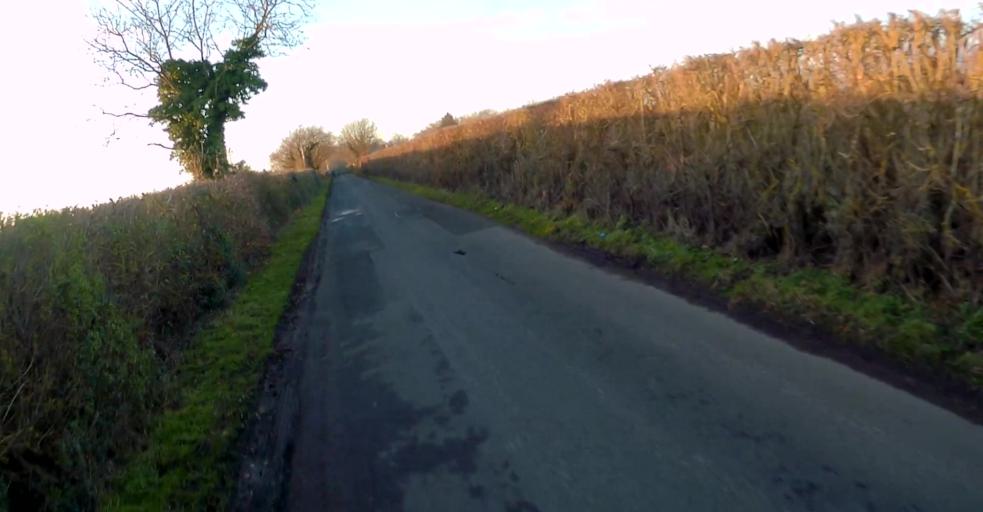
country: GB
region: England
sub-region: West Berkshire
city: Stratfield Mortimer
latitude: 51.3488
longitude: -1.0166
